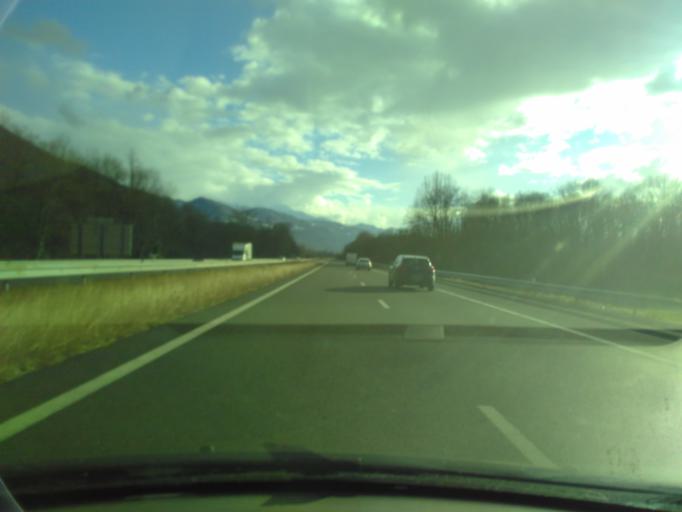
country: FR
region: Rhone-Alpes
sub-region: Departement de l'Isere
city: Goncelin
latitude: 45.3545
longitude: 5.9684
